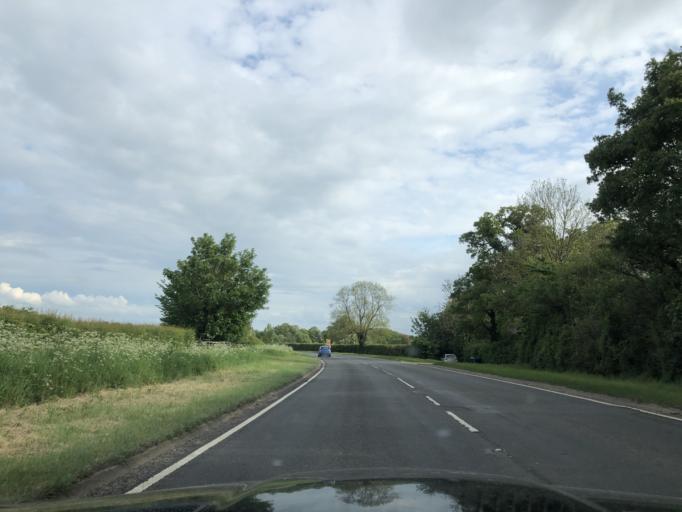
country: GB
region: England
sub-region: Warwickshire
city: Shipston on Stour
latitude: 52.1153
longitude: -1.6194
